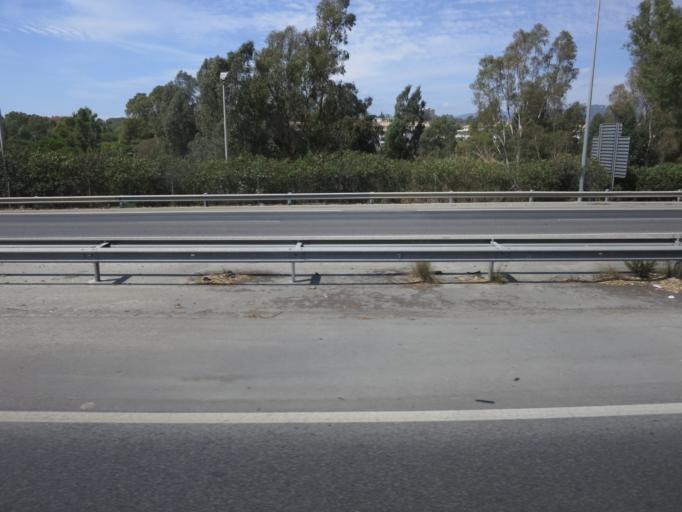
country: ES
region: Andalusia
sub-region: Provincia de Malaga
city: Marbella
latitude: 36.4993
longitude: -4.9472
